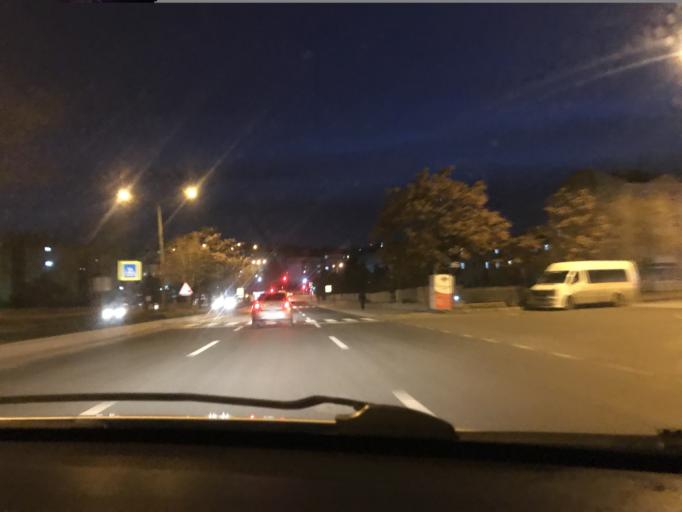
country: TR
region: Ankara
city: Batikent
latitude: 39.9598
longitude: 32.7304
